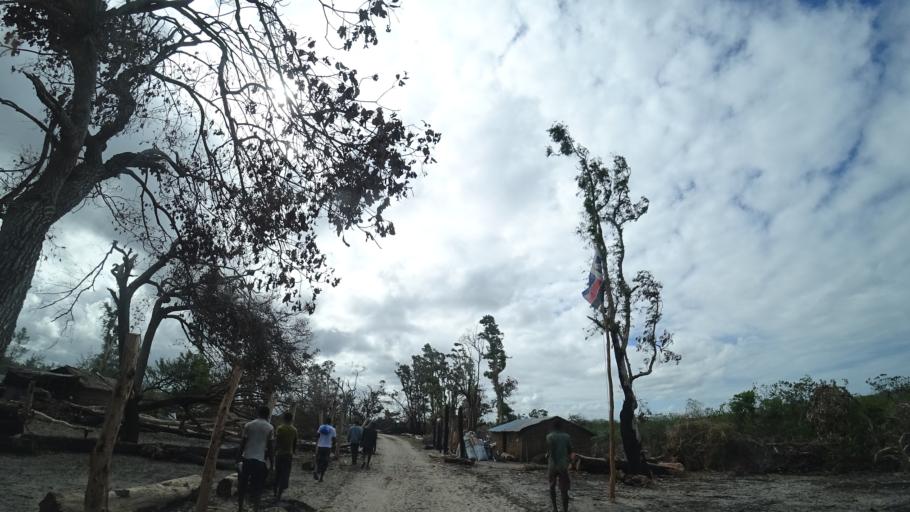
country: MZ
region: Sofala
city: Beira
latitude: -19.5762
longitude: 35.2629
